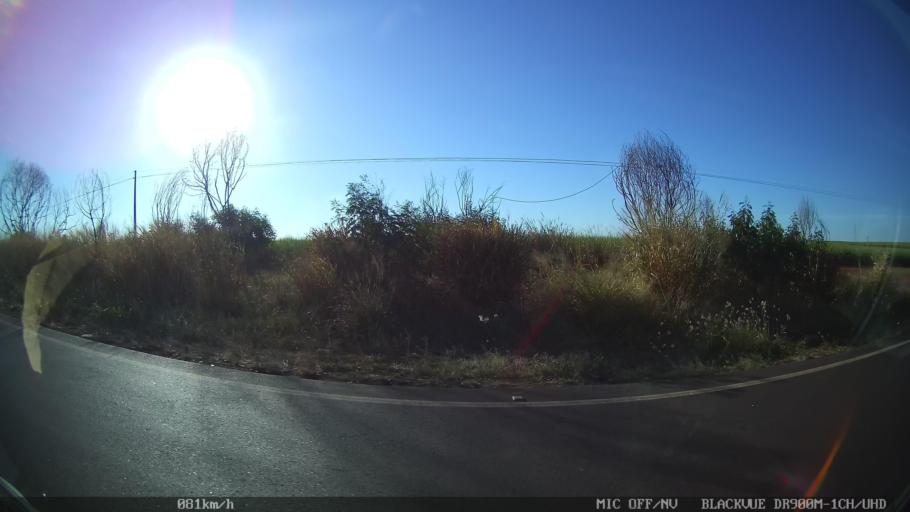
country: BR
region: Sao Paulo
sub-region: Guapiacu
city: Guapiacu
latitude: -20.7375
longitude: -49.0834
